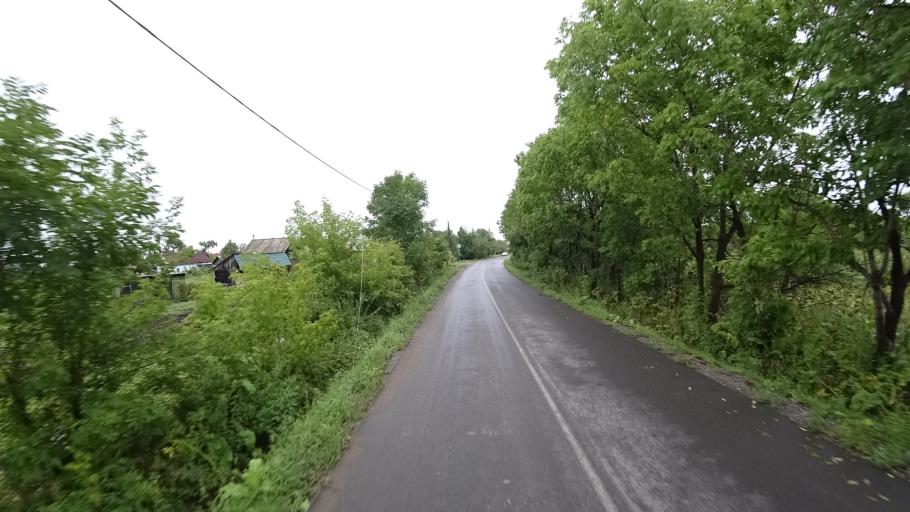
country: RU
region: Primorskiy
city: Monastyrishche
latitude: 44.2060
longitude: 132.4354
